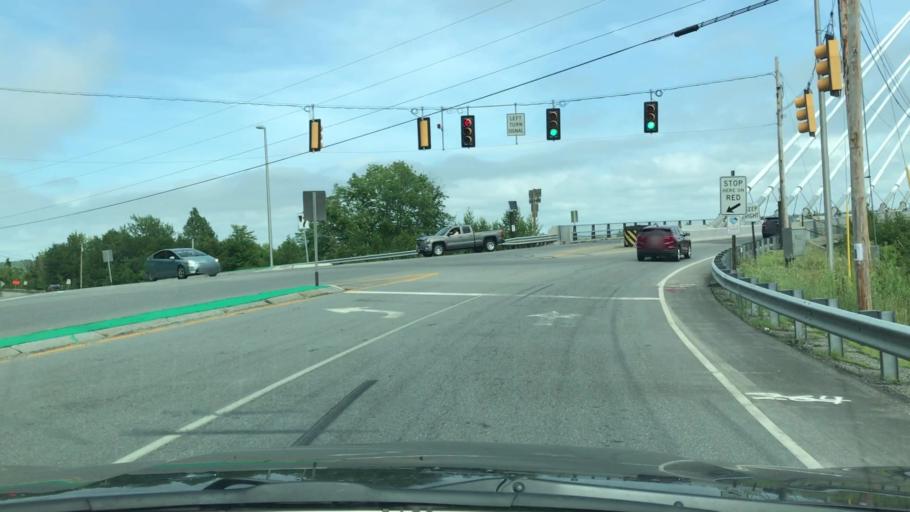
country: US
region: Maine
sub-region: Hancock County
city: Bucksport
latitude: 44.5610
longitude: -68.8062
